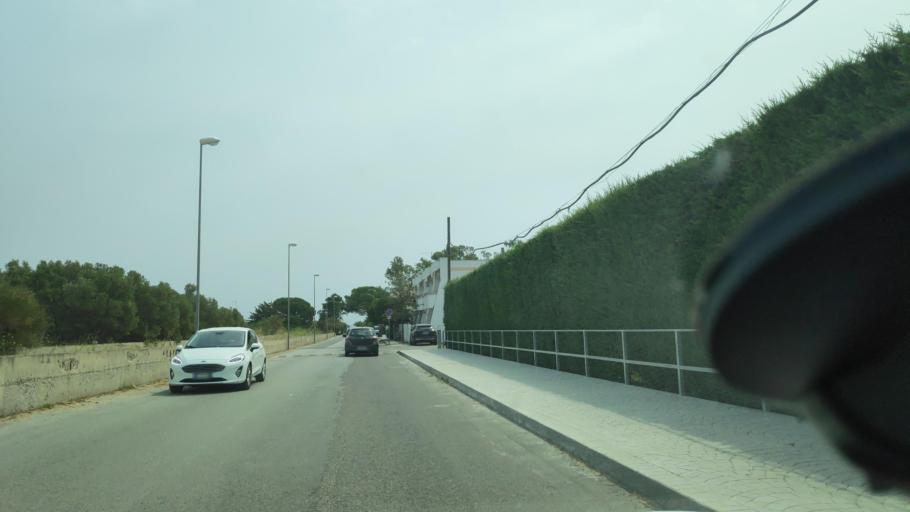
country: IT
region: Calabria
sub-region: Provincia di Catanzaro
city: Sant'Andrea Ionio Marina
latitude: 38.6174
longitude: 16.5574
